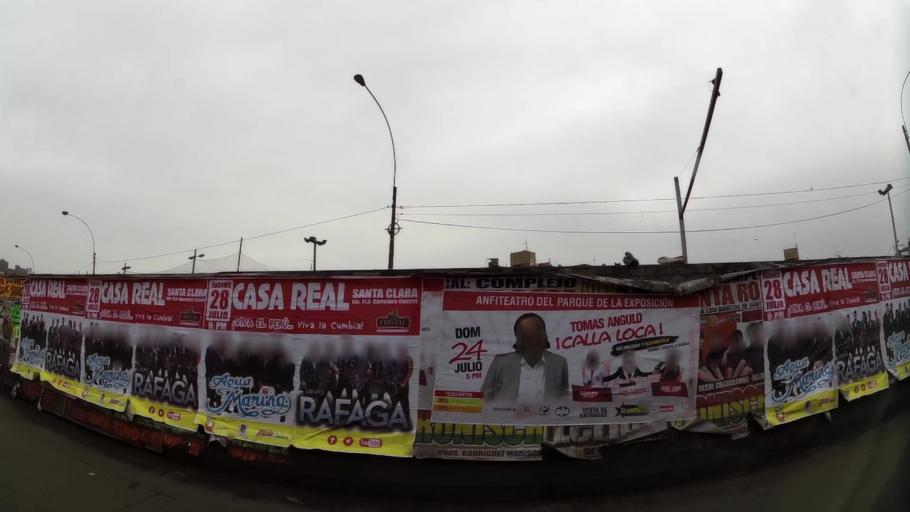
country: PE
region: Lima
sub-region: Lima
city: San Luis
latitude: -12.0573
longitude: -77.0075
